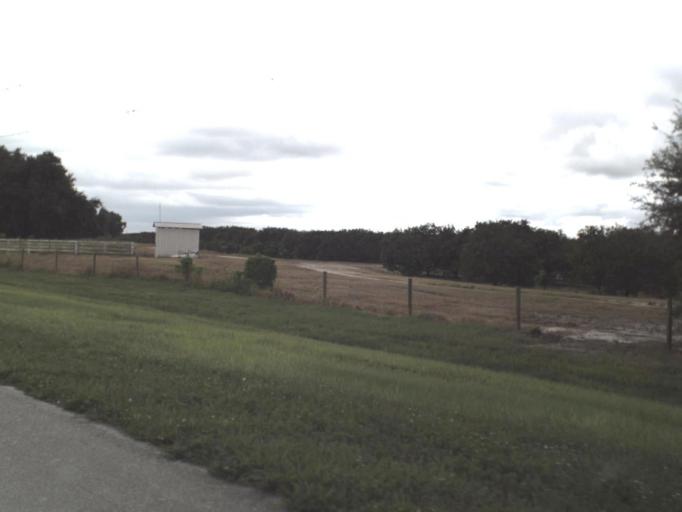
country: US
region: Florida
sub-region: Hillsborough County
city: Balm
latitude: 27.5886
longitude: -82.0943
